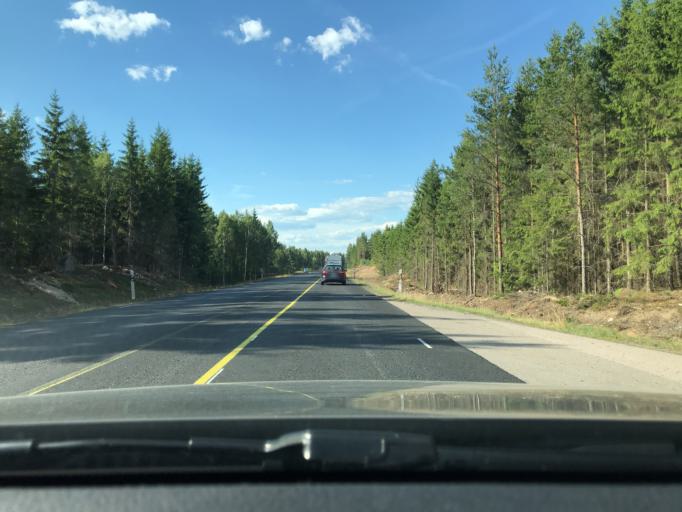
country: SE
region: Kronoberg
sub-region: Almhults Kommun
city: AElmhult
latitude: 56.5686
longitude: 14.1839
